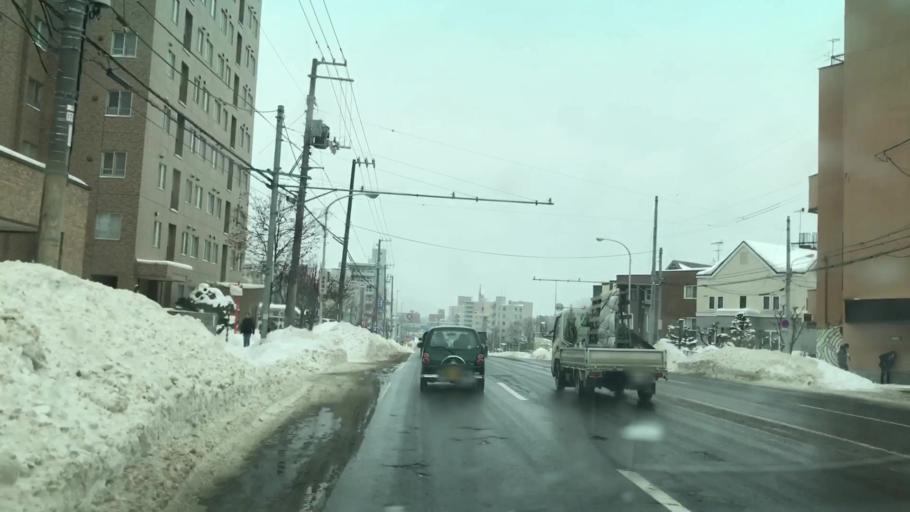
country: JP
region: Hokkaido
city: Sapporo
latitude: 43.0319
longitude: 141.3635
